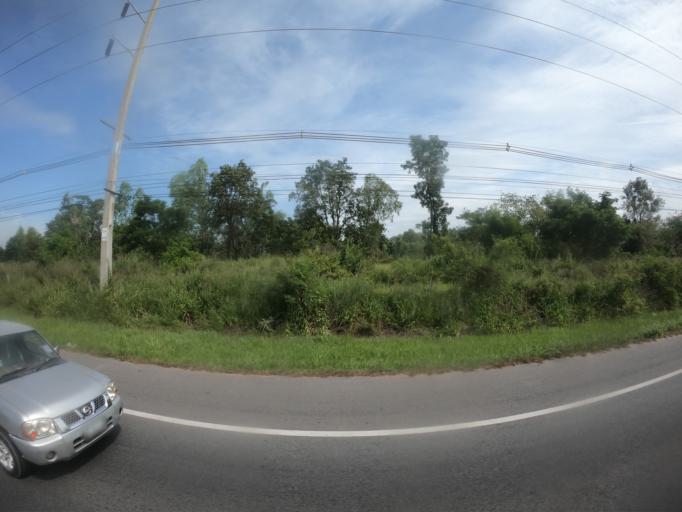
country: TH
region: Maha Sarakham
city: Chiang Yuen
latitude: 16.4355
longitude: 103.0528
